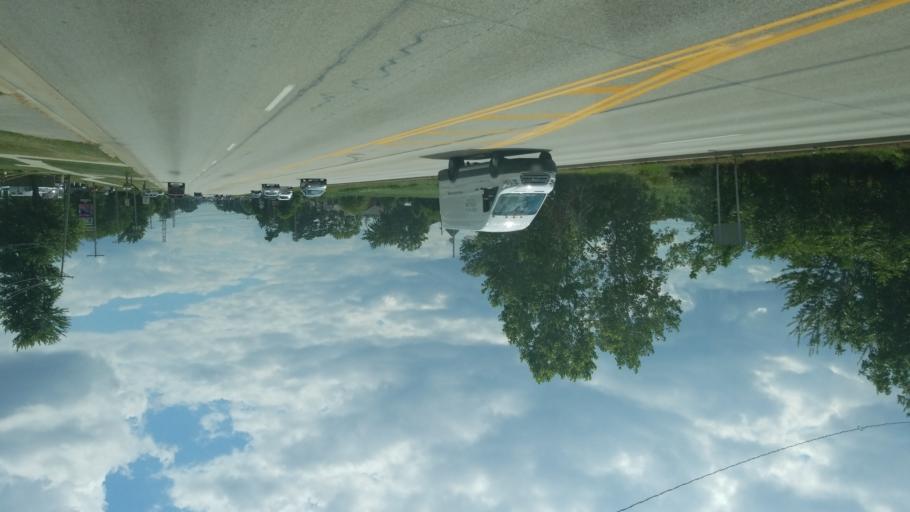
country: US
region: Ohio
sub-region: Wood County
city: Northwood
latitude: 41.6374
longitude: -83.4490
